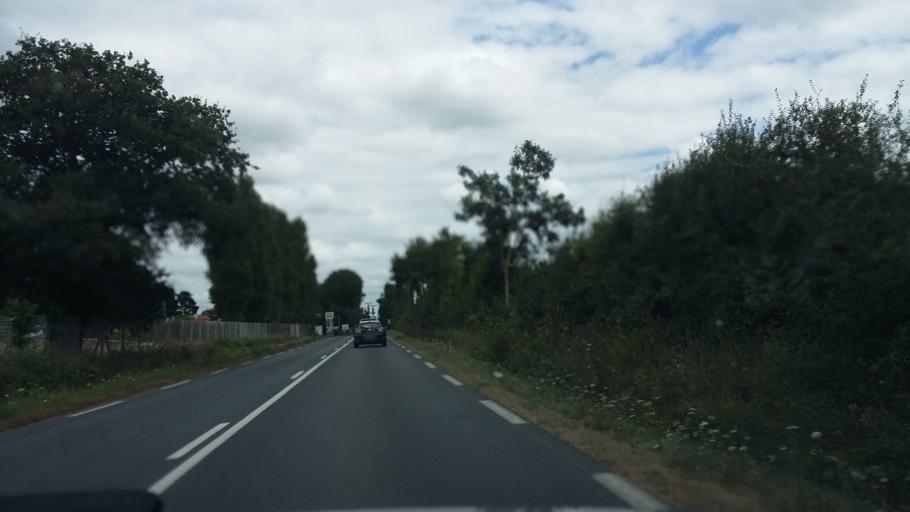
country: FR
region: Pays de la Loire
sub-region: Departement de la Vendee
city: Saint-Christophe-du-Ligneron
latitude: 46.8232
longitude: -1.7756
